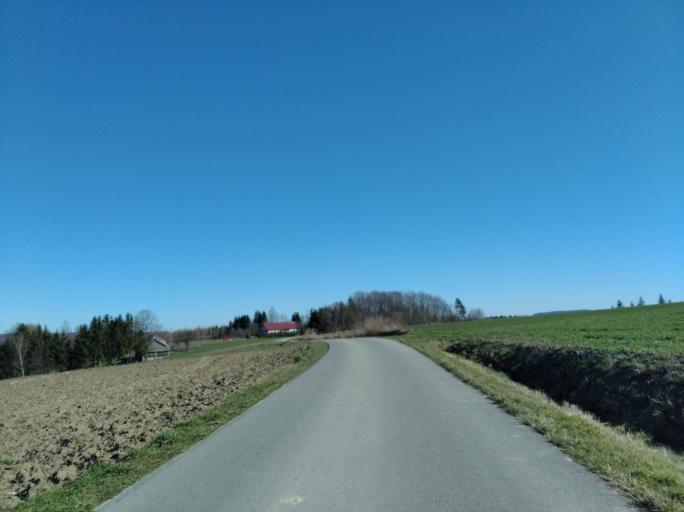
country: PL
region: Subcarpathian Voivodeship
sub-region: Powiat strzyzowski
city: Wisniowa
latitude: 49.9036
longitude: 21.7043
